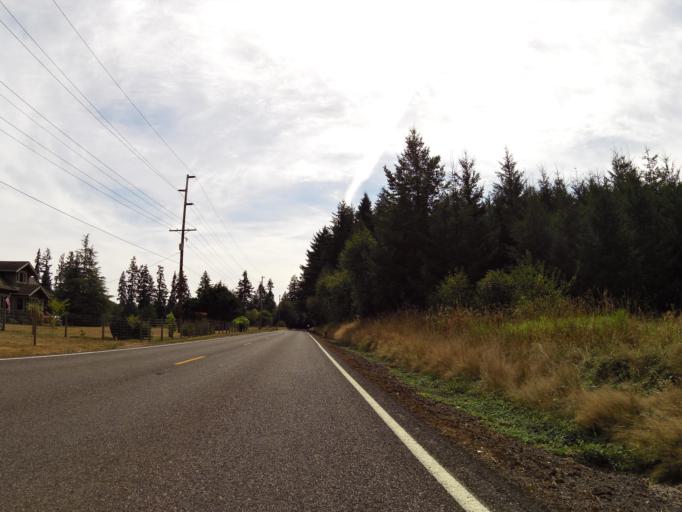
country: US
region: Washington
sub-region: Lewis County
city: Winlock
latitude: 46.4359
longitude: -122.9701
